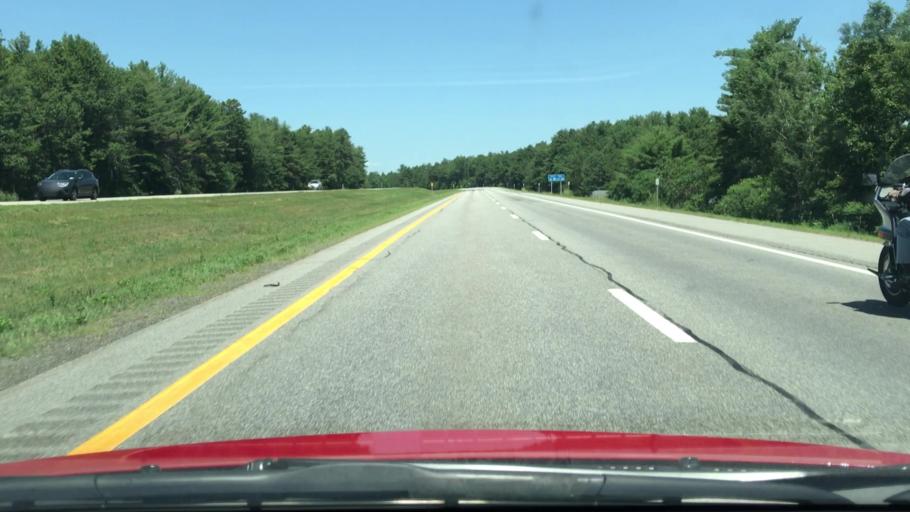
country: US
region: New York
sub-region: Essex County
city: Keeseville
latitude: 44.4822
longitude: -73.4890
